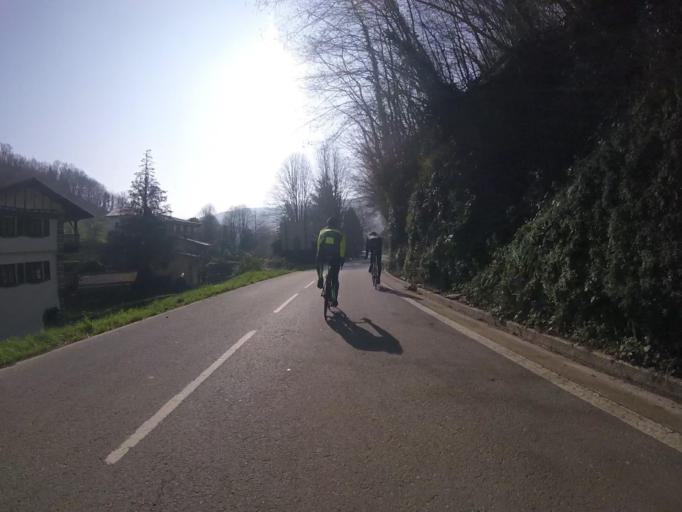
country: ES
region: Navarre
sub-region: Provincia de Navarra
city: Bera
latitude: 43.2842
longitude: -1.6795
